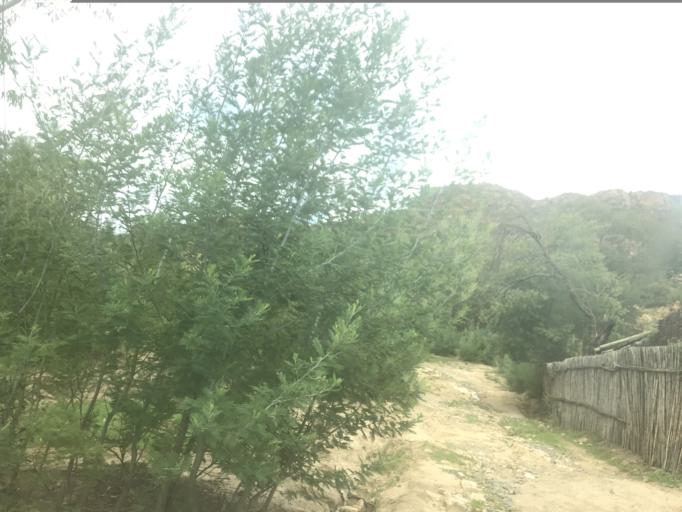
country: LS
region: Maseru
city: Nako
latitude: -29.6314
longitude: 27.5138
